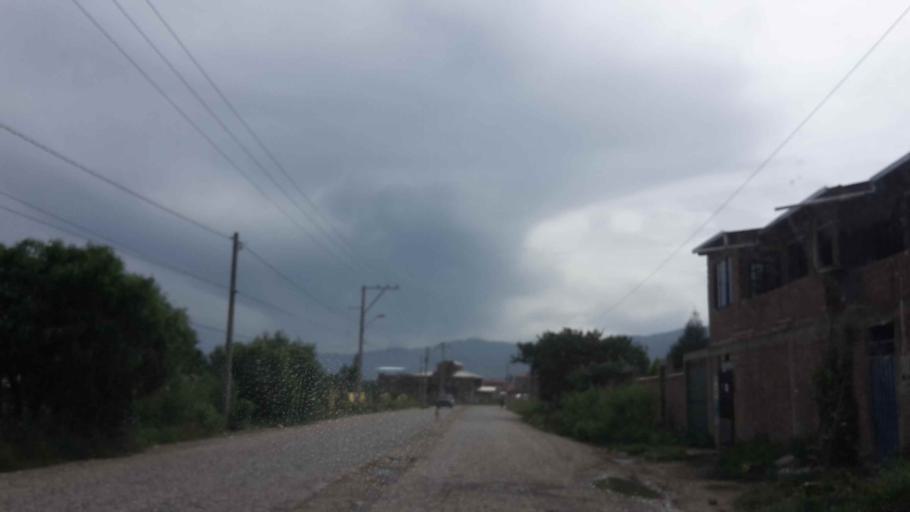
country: BO
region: Cochabamba
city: Cochabamba
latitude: -17.3358
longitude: -66.2571
